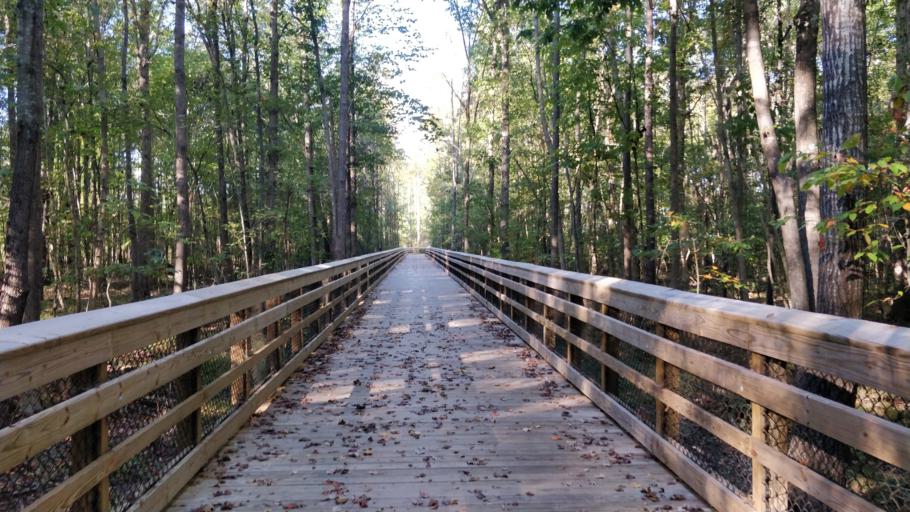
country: US
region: North Carolina
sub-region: Wake County
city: Morrisville
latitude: 35.8171
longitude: -78.8303
